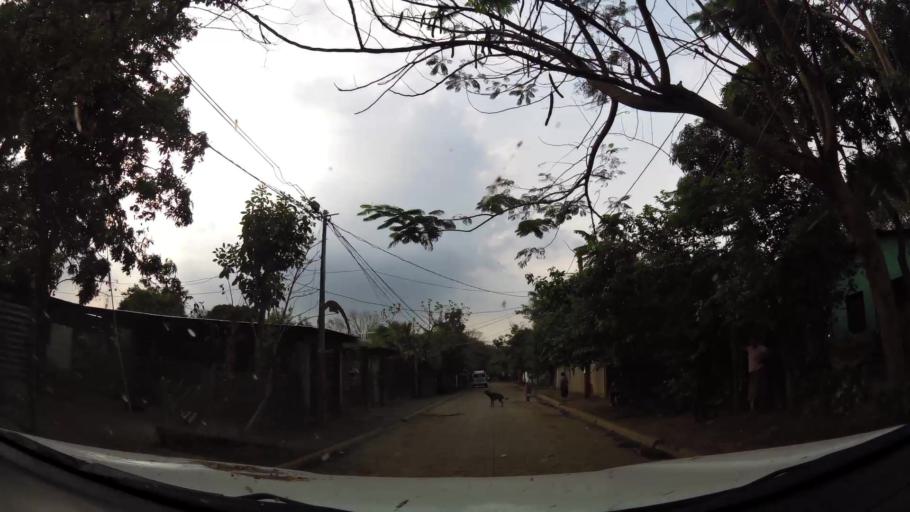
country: NI
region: Masaya
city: Masaya
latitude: 11.9855
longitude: -86.1056
